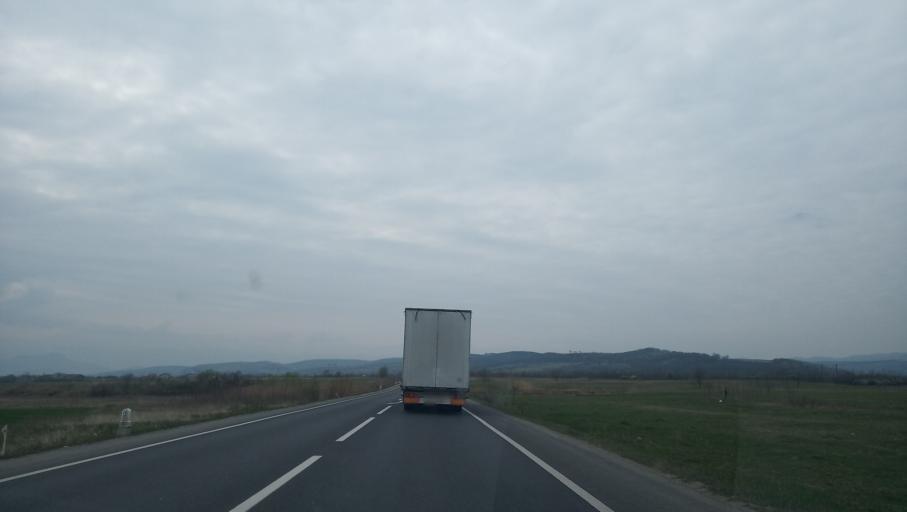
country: RO
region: Hunedoara
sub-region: Comuna Calan
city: Calan
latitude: 45.7109
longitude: 22.9918
